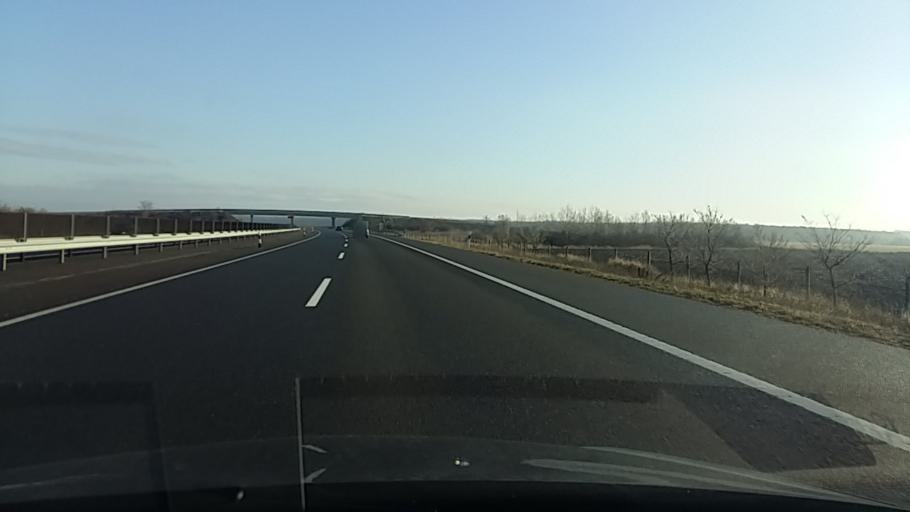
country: HU
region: Hajdu-Bihar
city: Gorbehaza
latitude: 47.8080
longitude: 21.1653
